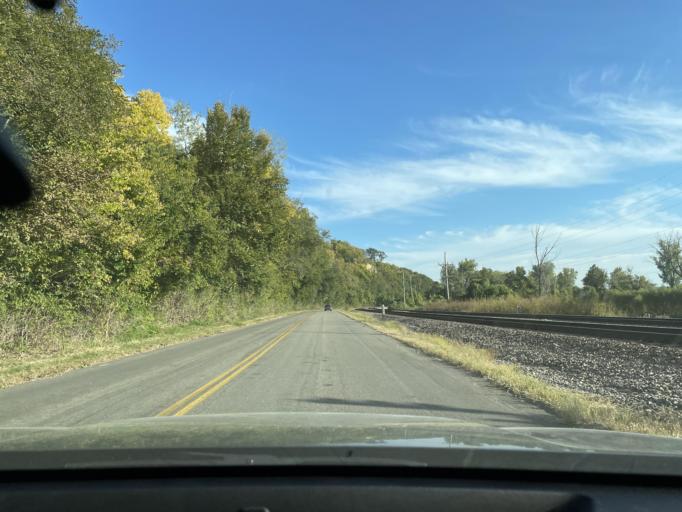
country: US
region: Kansas
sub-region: Doniphan County
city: Elwood
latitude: 39.7752
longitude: -94.8671
